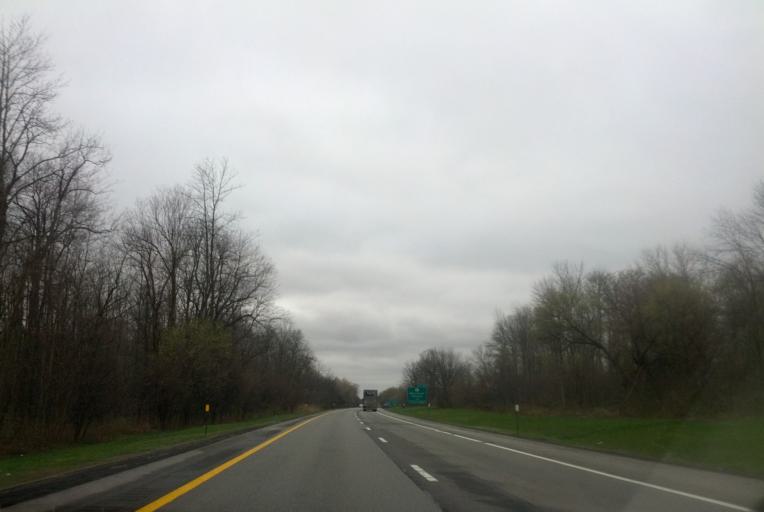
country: US
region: New York
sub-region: Ontario County
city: Shortsville
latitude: 42.9770
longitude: -77.1999
